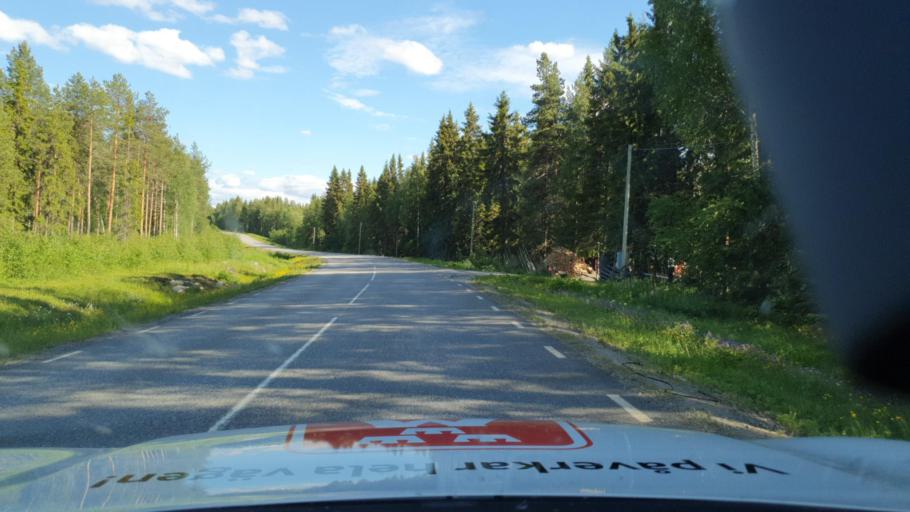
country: SE
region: Vaesterbotten
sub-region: Norsjo Kommun
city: Norsjoe
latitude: 64.8379
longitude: 19.7663
